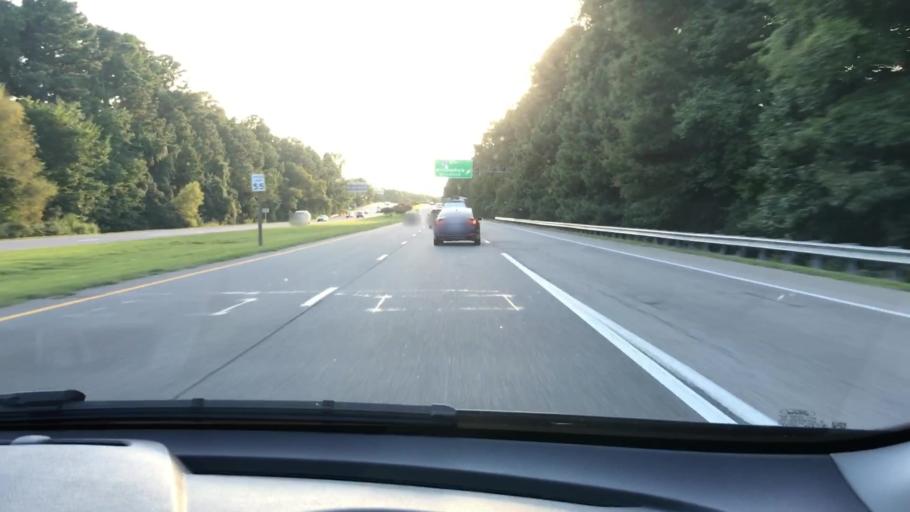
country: US
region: Virginia
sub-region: City of Hampton
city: Hampton
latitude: 37.0600
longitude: -76.4104
